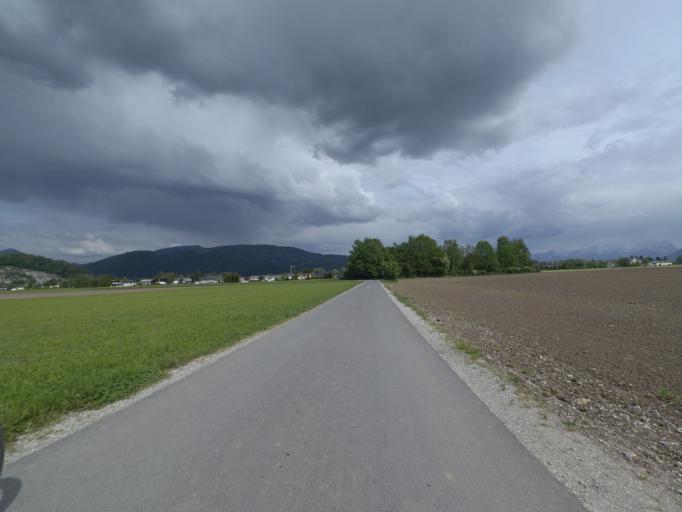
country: AT
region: Salzburg
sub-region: Politischer Bezirk Salzburg-Umgebung
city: Anif
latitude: 47.7508
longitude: 13.0550
